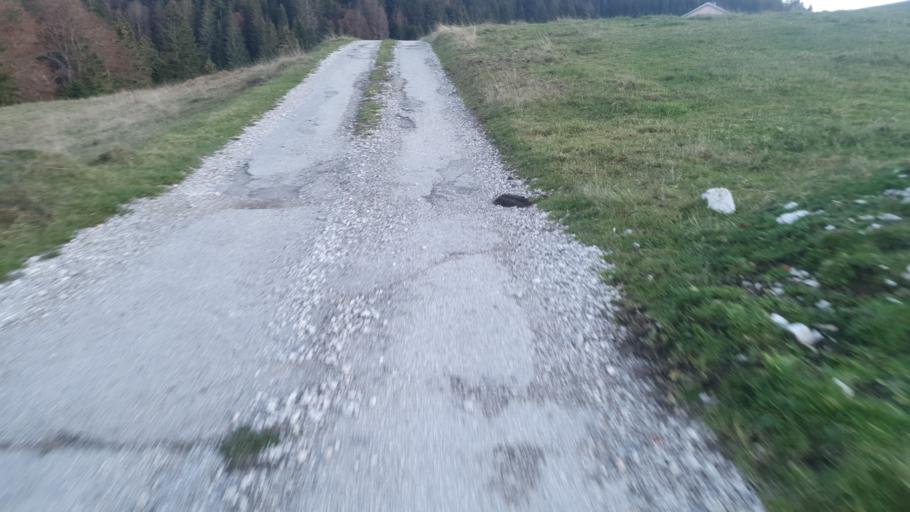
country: FR
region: Franche-Comte
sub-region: Departement du Jura
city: Saint-Claude
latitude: 46.3075
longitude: 5.8528
